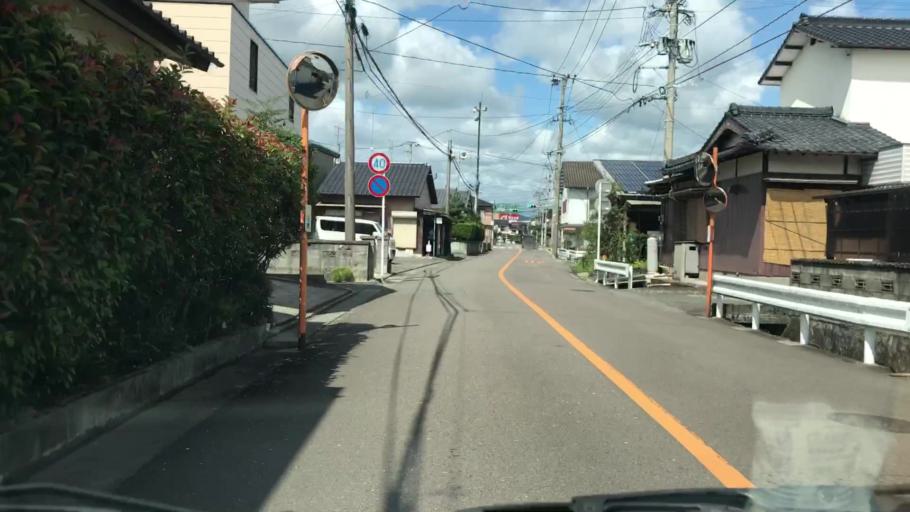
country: JP
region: Saga Prefecture
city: Saga-shi
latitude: 33.2451
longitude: 130.2030
